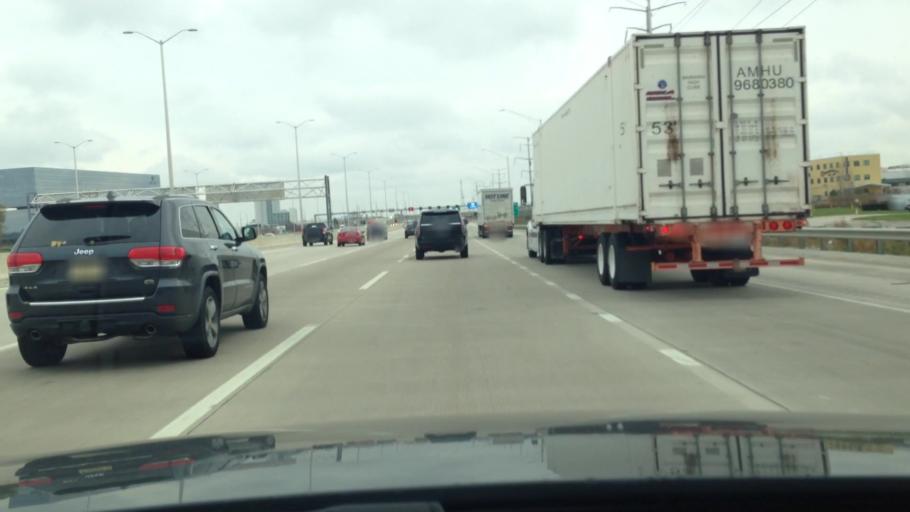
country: US
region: Illinois
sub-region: Cook County
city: Hoffman Estates
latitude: 42.0606
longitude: -88.0554
